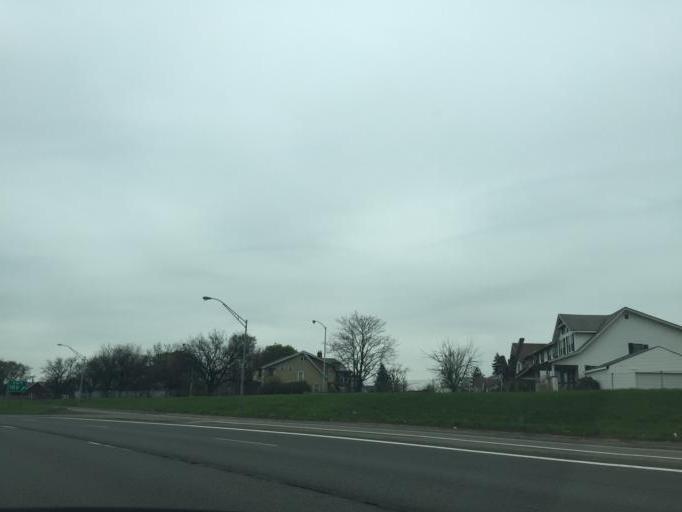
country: US
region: Michigan
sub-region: Wayne County
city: Dearborn
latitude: 42.3694
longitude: -83.1437
